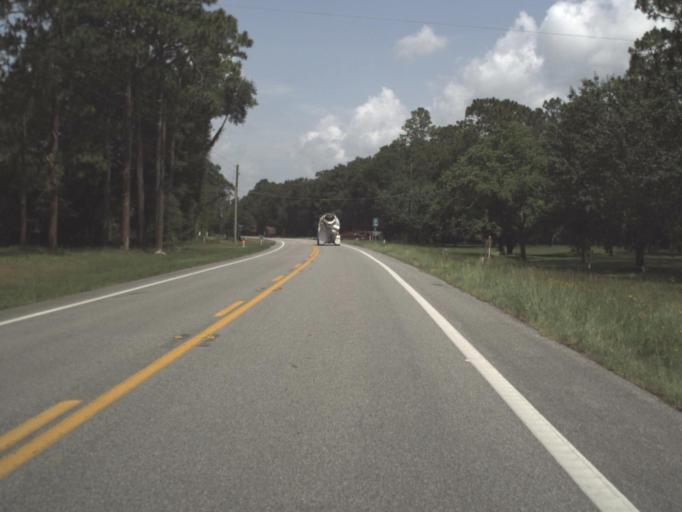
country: US
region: Florida
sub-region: Madison County
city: Madison
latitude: 30.4338
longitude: -83.3158
